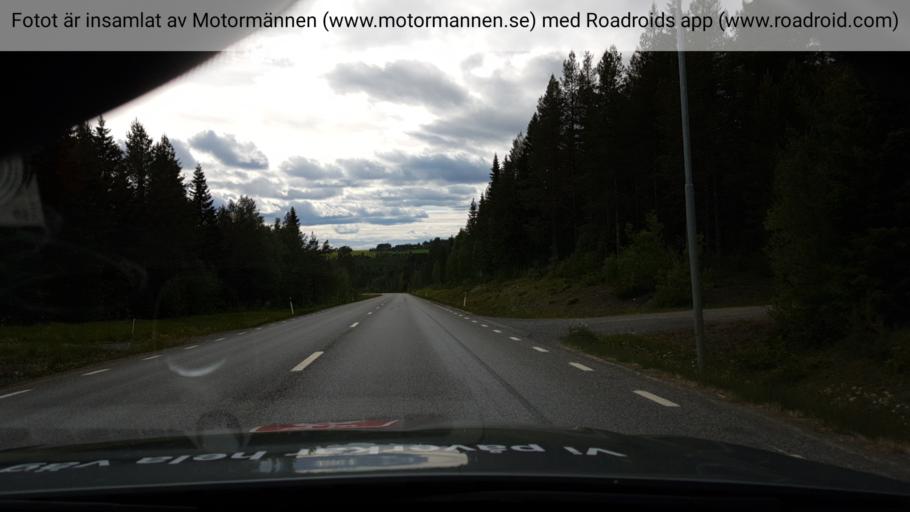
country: SE
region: Jaemtland
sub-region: OEstersunds Kommun
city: Lit
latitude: 63.3966
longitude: 14.9994
